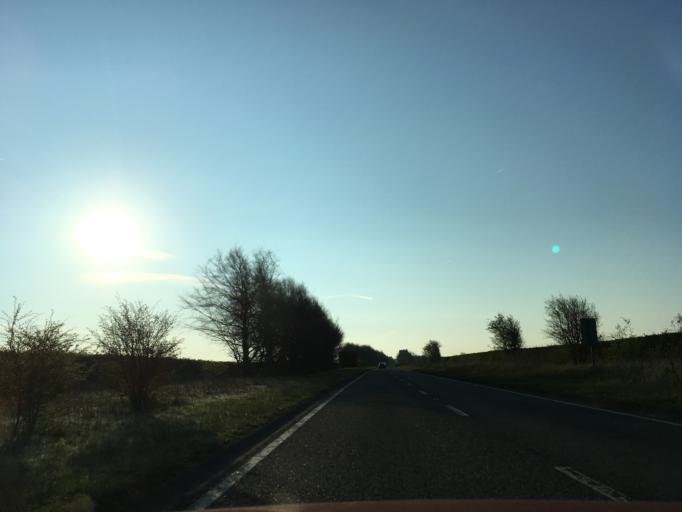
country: GB
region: England
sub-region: Gloucestershire
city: Northleach
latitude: 51.8419
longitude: -1.8479
